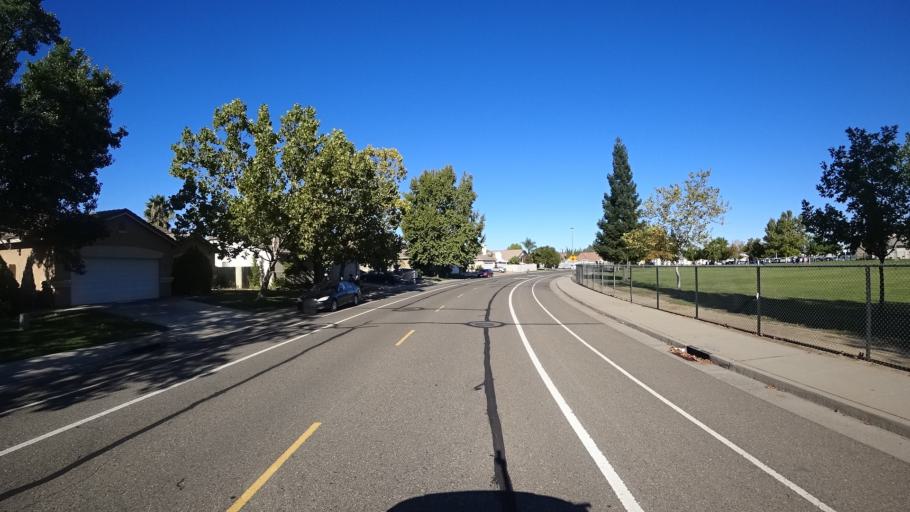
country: US
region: California
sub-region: Sacramento County
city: Elk Grove
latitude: 38.4413
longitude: -121.3850
